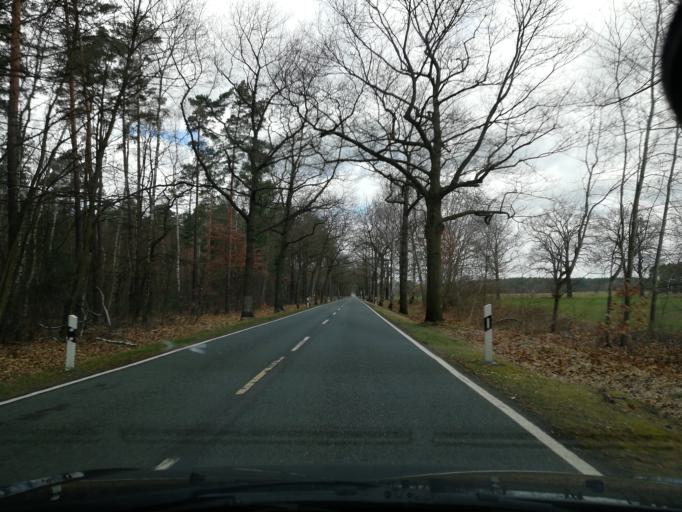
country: DE
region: Brandenburg
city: Altdobern
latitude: 51.6999
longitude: 14.0761
